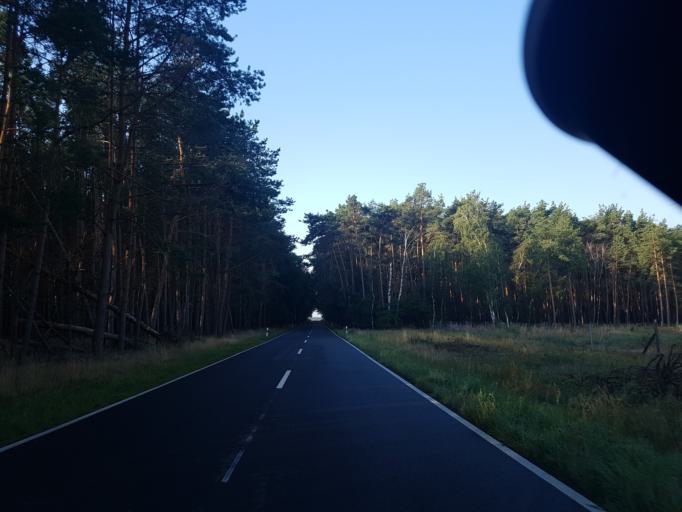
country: DE
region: Saxony-Anhalt
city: Holzdorf
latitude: 51.8025
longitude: 13.1361
